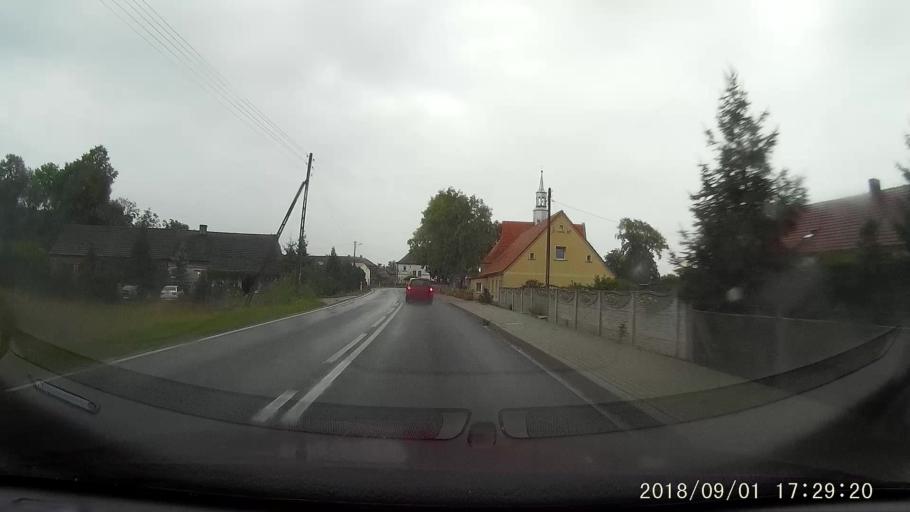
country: PL
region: Lubusz
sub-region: Powiat zaganski
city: Zagan
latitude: 51.6513
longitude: 15.3164
